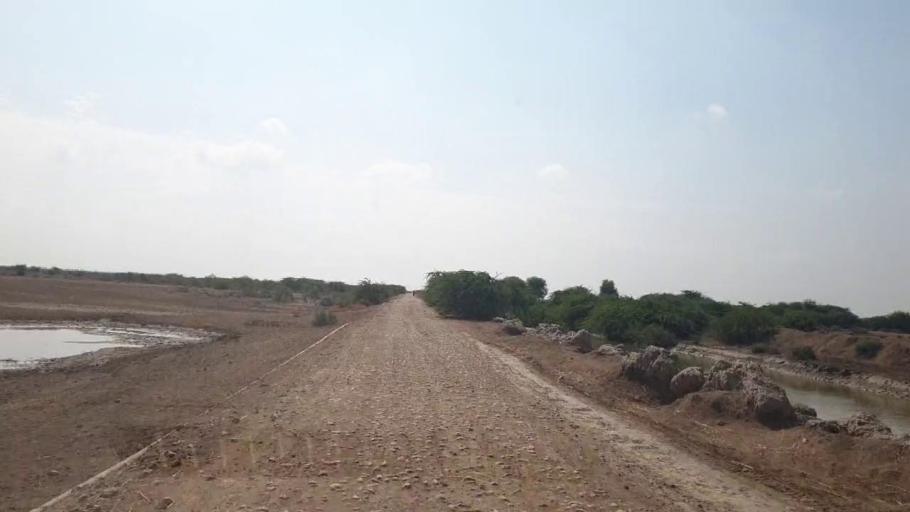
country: PK
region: Sindh
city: Badin
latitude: 24.5140
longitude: 68.6081
